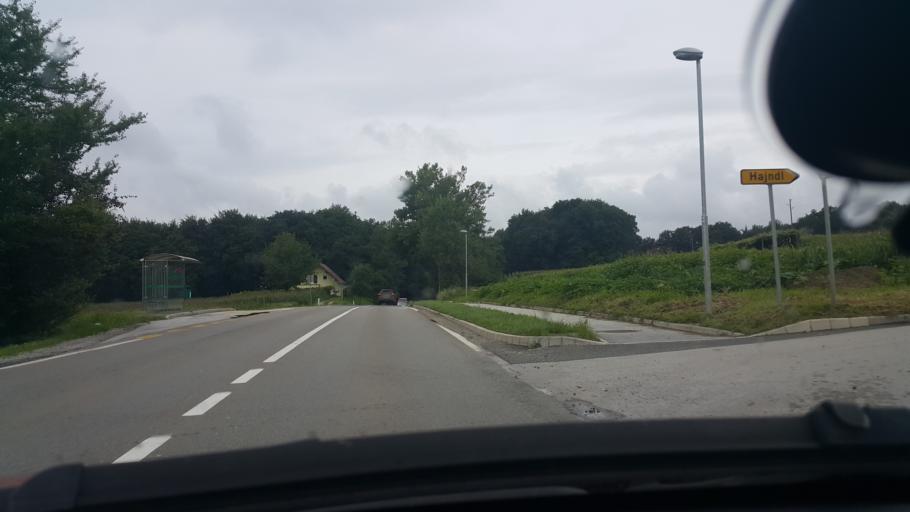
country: SI
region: Ormoz
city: Ormoz
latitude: 46.4098
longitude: 16.1235
